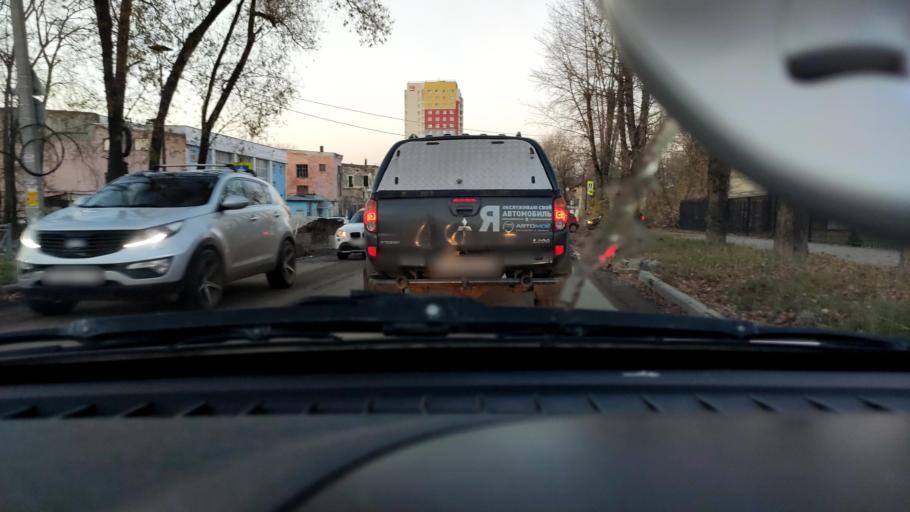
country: RU
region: Perm
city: Froly
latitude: 57.9681
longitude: 56.2735
